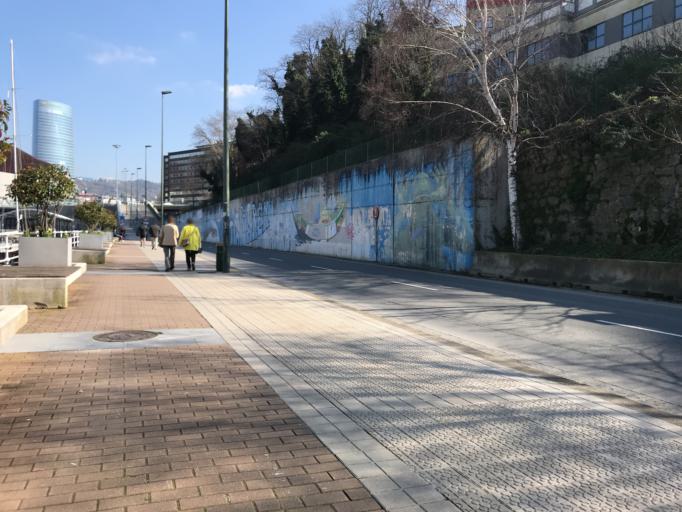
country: ES
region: Basque Country
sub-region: Bizkaia
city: Bilbao
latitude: 43.2658
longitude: -2.9491
